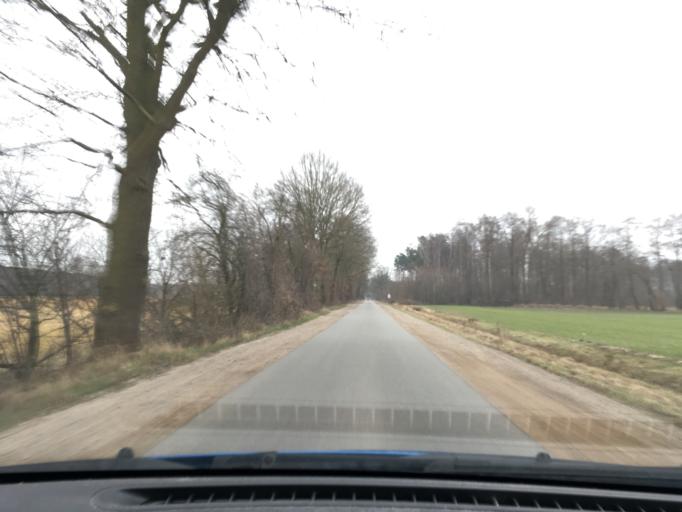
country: DE
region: Lower Saxony
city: Vogelsen
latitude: 53.2951
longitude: 10.3362
